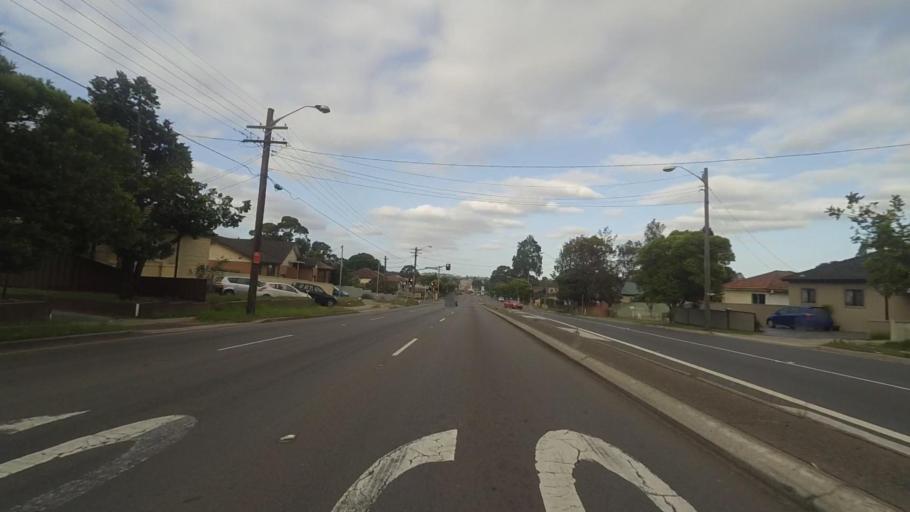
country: AU
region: New South Wales
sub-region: Bankstown
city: Revesby
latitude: -33.9355
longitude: 151.0240
